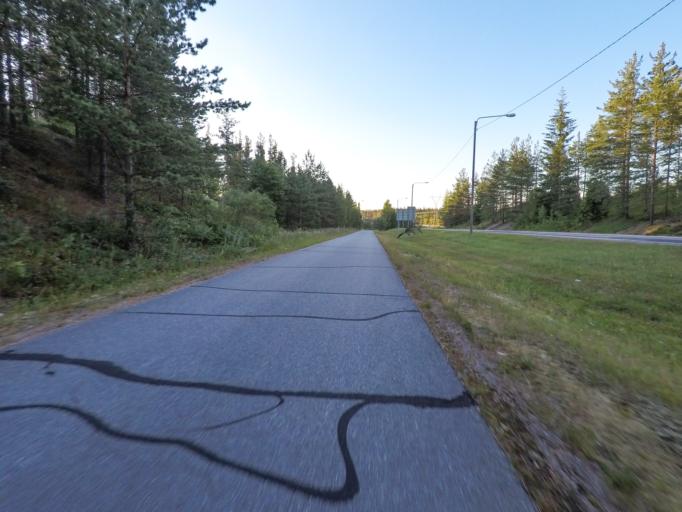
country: FI
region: South Karelia
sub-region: Imatra
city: Ruokolahti
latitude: 61.2575
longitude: 28.8792
